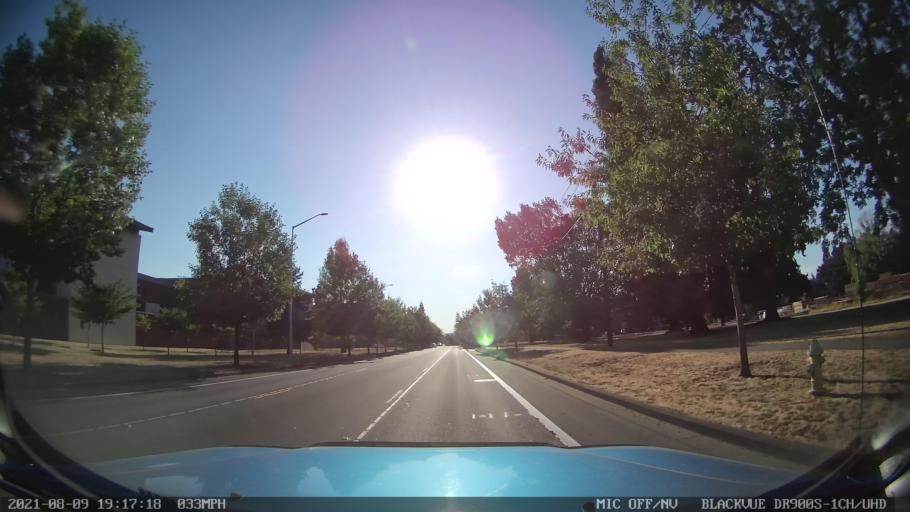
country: US
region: Oregon
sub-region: Marion County
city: Four Corners
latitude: 44.9399
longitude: -123.0023
